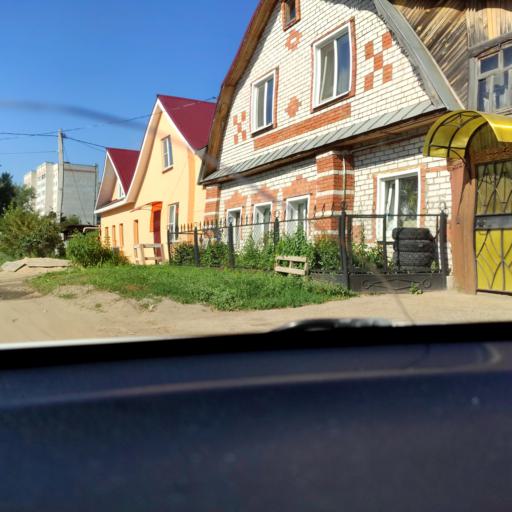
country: RU
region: Tatarstan
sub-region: Gorod Kazan'
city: Kazan
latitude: 55.7956
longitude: 49.0591
